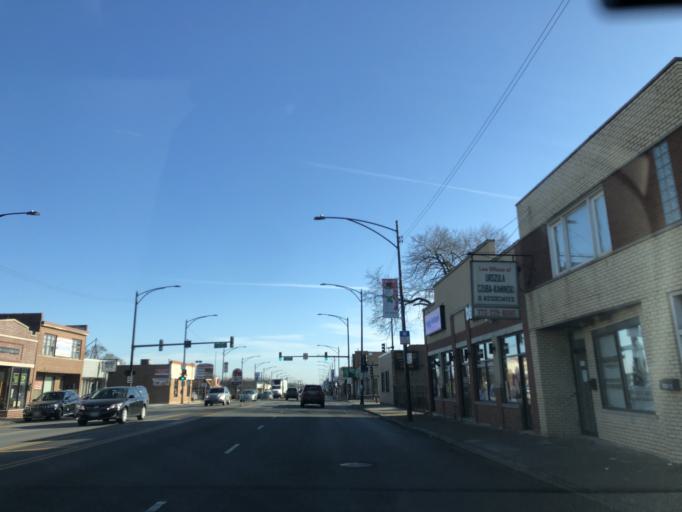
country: US
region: Illinois
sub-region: Cook County
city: Summit
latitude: 41.7920
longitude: -87.7974
